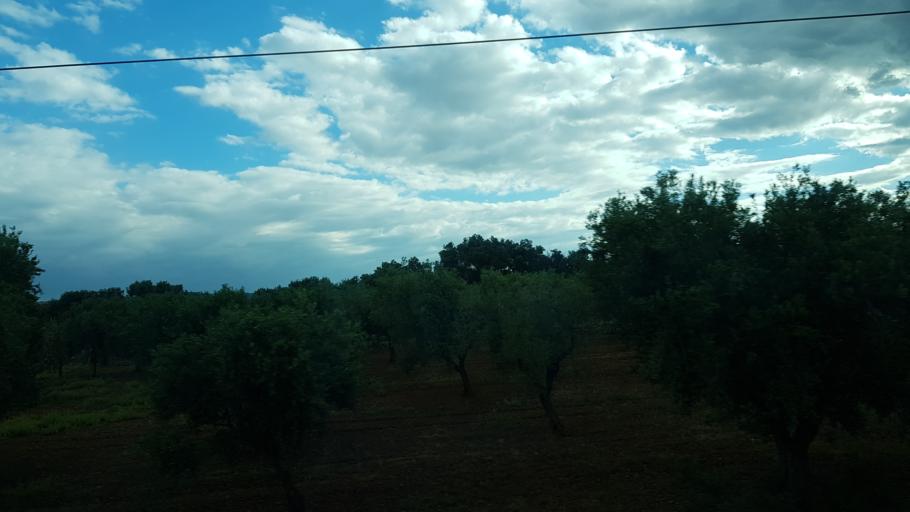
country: IT
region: Apulia
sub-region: Provincia di Brindisi
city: Pezze di Greco
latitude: 40.8423
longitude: 17.4011
